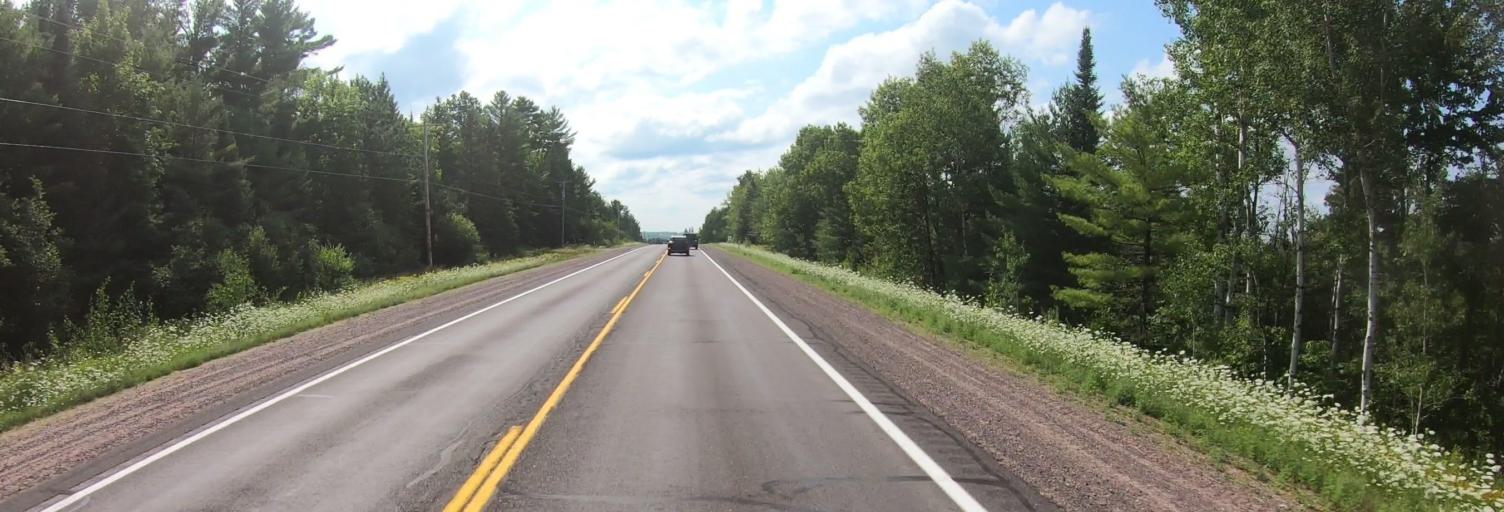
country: US
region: Michigan
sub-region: Ontonagon County
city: Ontonagon
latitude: 46.5348
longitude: -89.2516
